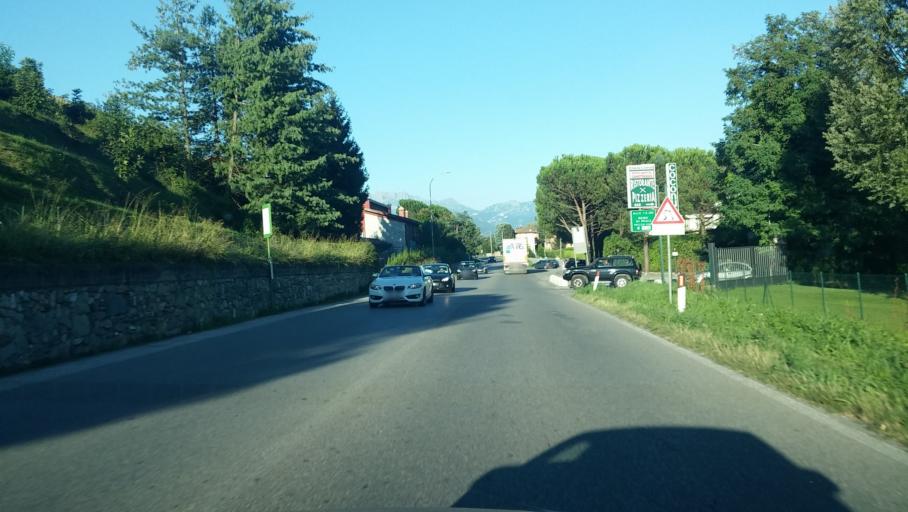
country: IT
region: Lombardy
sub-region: Provincia di Como
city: Longone al Segrino
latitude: 45.8074
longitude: 9.2553
